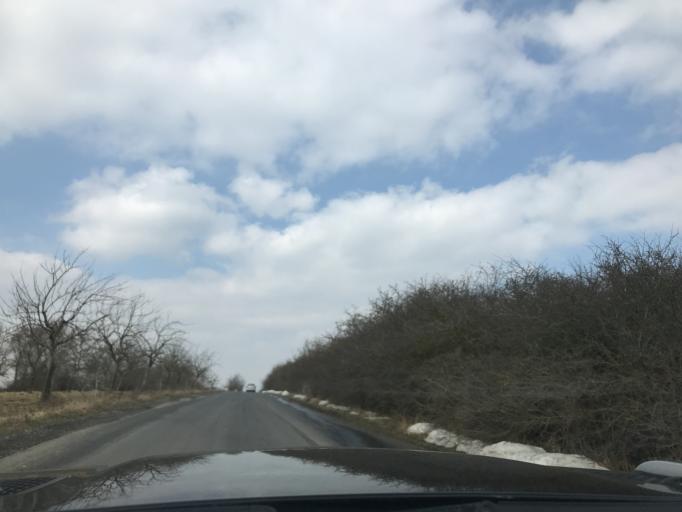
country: DE
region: Thuringia
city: Muehlhausen
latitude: 51.2180
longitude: 10.3987
